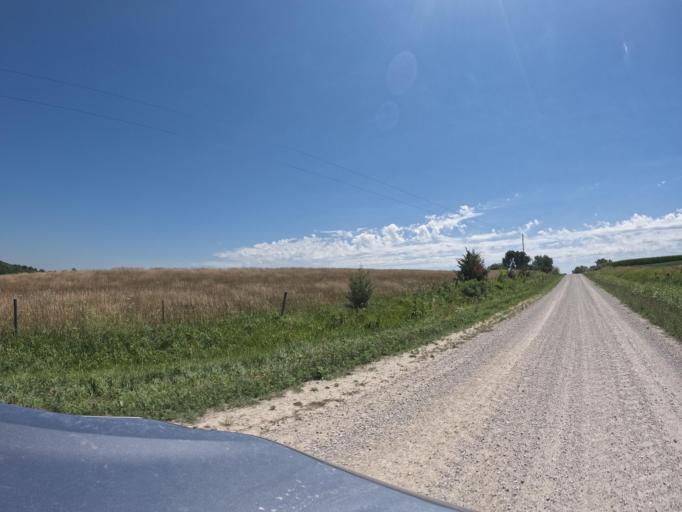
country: US
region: Iowa
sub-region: Keokuk County
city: Sigourney
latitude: 41.4172
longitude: -92.3164
